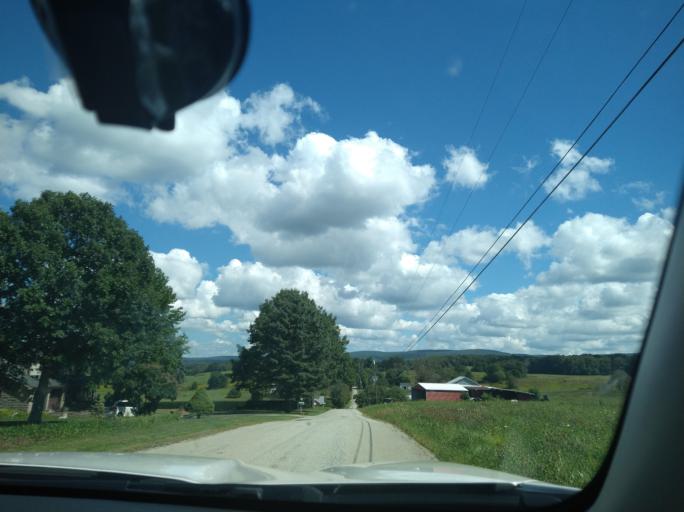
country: US
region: Pennsylvania
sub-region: Fayette County
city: Bear Rocks
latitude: 40.1032
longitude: -79.3502
